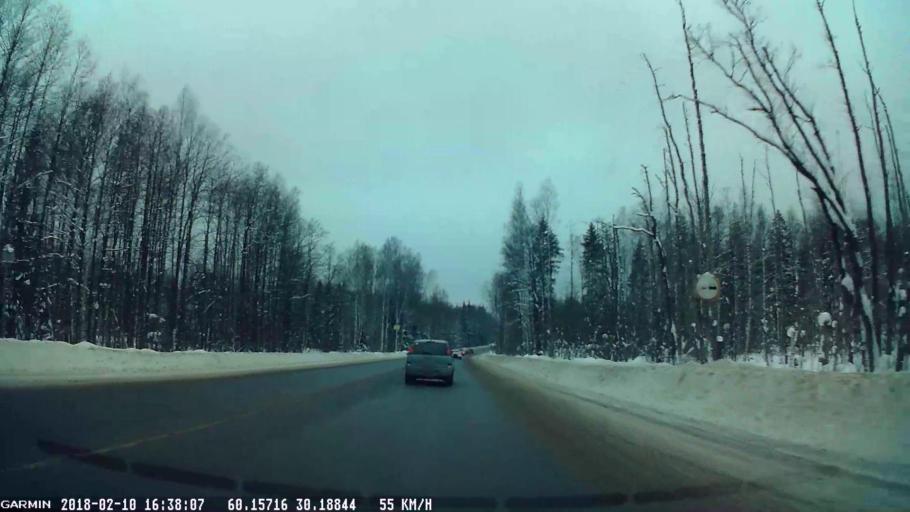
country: RU
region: Leningrad
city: Sertolovo
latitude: 60.1528
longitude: 30.1940
